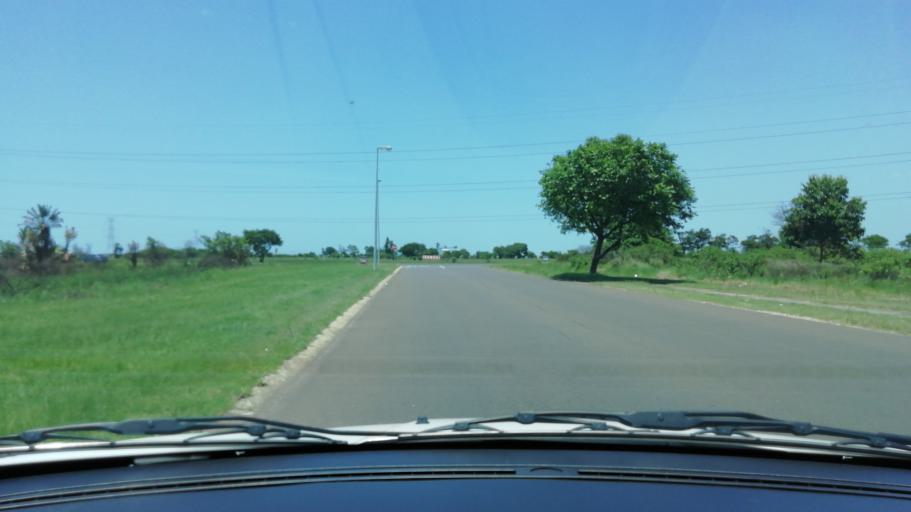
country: ZA
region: KwaZulu-Natal
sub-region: uThungulu District Municipality
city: Richards Bay
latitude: -28.7388
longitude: 32.0470
